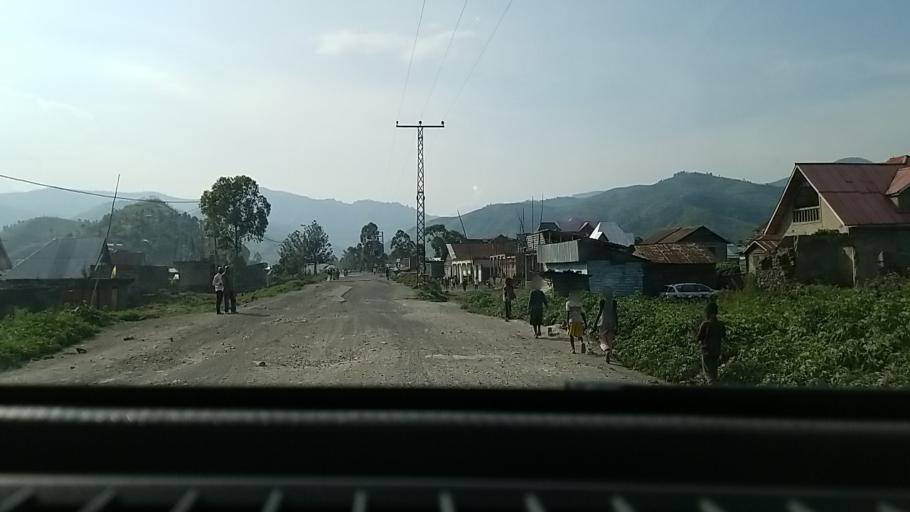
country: CD
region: Nord Kivu
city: Sake
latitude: -1.5734
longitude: 29.0623
